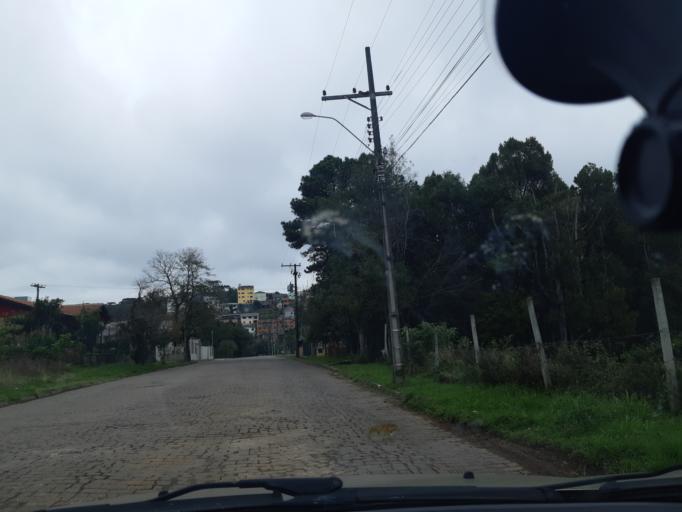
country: BR
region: Rio Grande do Sul
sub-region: Caxias Do Sul
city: Caxias do Sul
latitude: -29.1583
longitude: -51.2053
